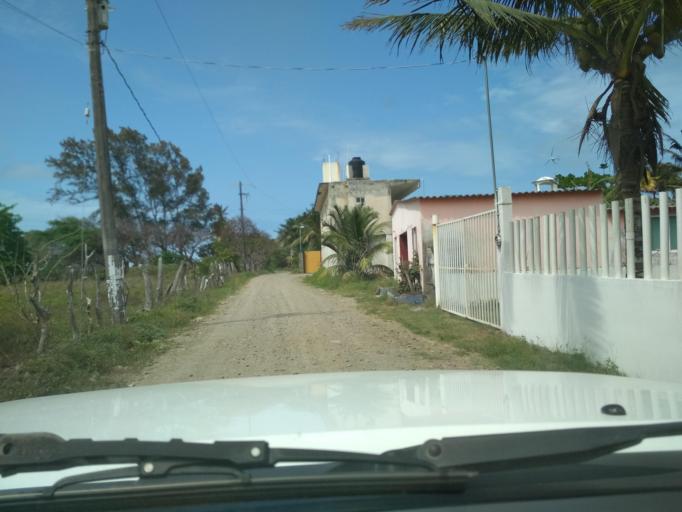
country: MX
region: Veracruz
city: Anton Lizardo
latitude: 19.0241
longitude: -95.9679
